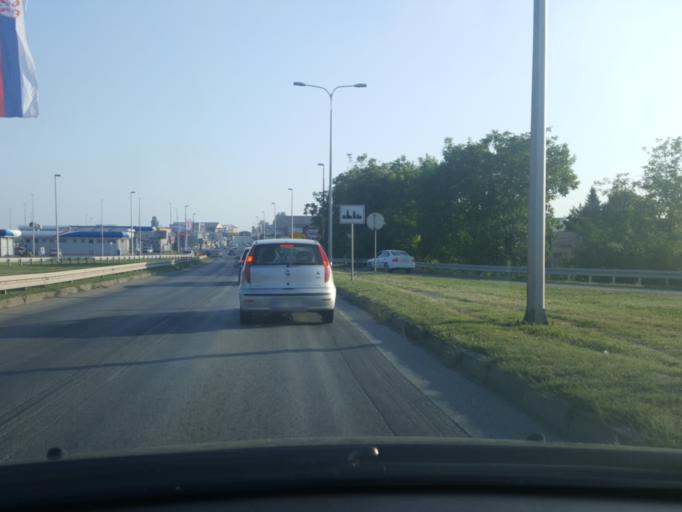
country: RS
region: Central Serbia
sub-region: Macvanski Okrug
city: Sabac
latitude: 44.7536
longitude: 19.7073
